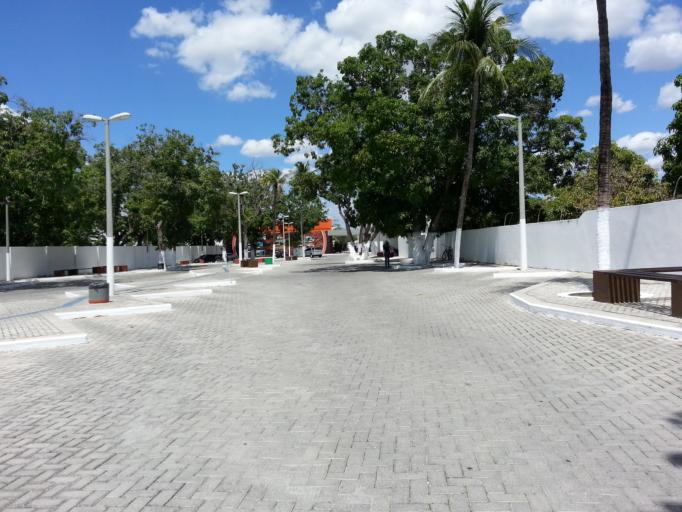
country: BR
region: Ceara
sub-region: Quixada
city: Quixada
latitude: -4.9753
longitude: -39.0157
